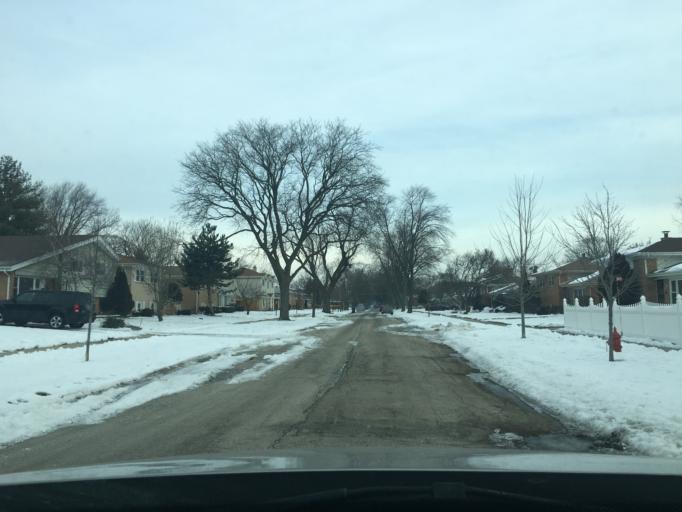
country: US
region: Illinois
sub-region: Cook County
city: Des Plaines
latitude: 42.0149
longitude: -87.8931
